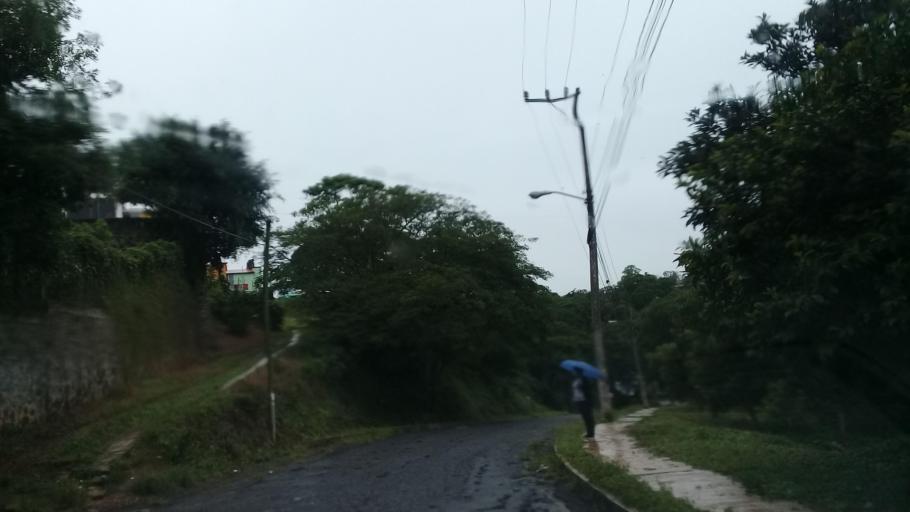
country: MX
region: Veracruz
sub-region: Xalapa
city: Lomas Verdes
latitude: 19.5141
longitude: -96.8996
